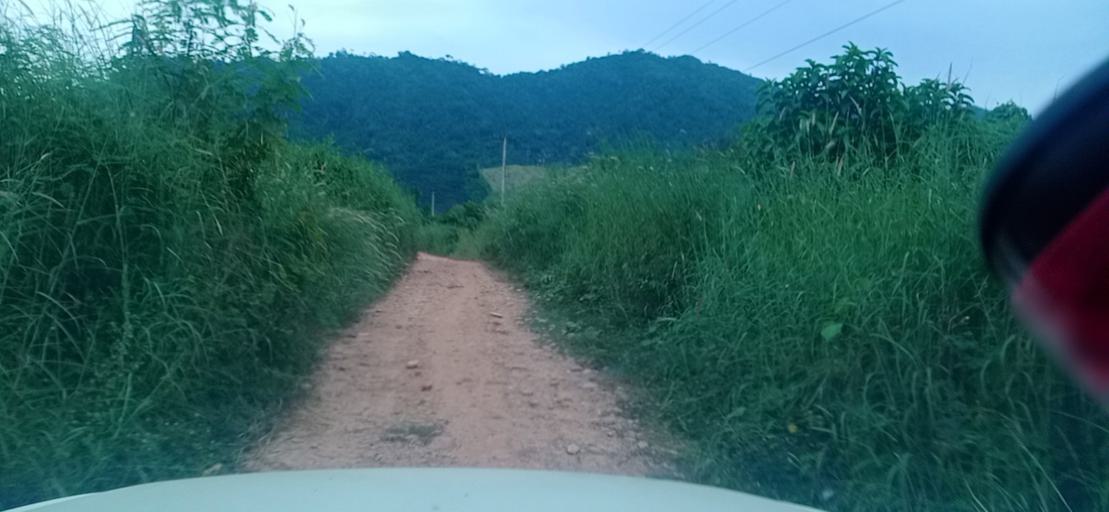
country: TH
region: Changwat Bueng Kan
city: Pak Khat
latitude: 18.5652
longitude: 103.3066
